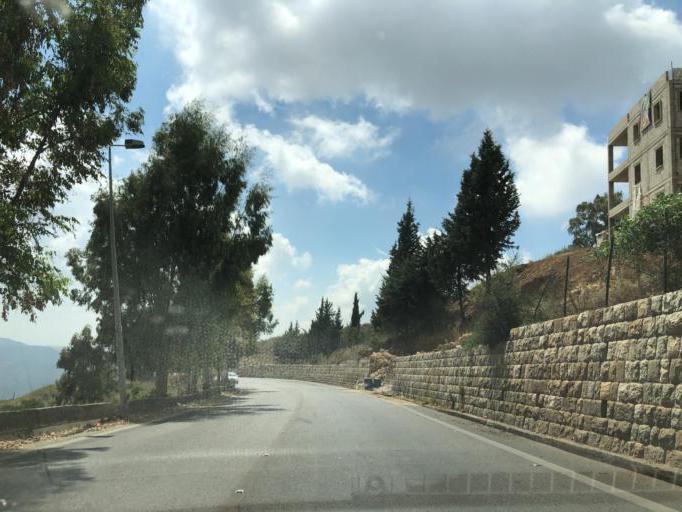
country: LB
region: Mont-Liban
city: Beit ed Dine
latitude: 33.6957
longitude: 35.5511
